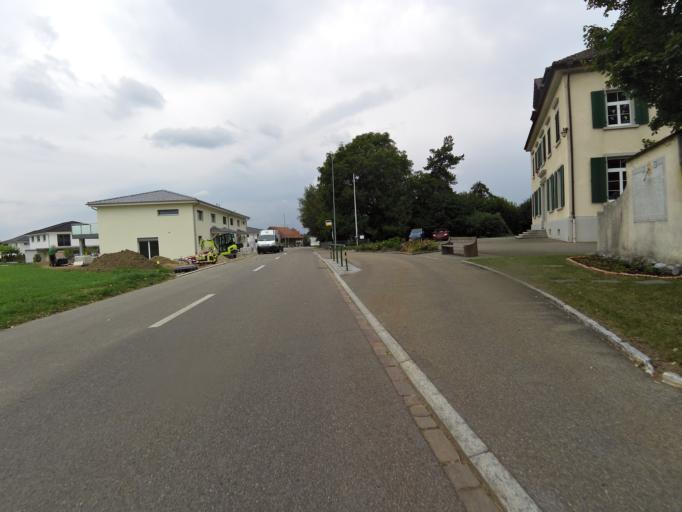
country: CH
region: Thurgau
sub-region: Frauenfeld District
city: Homburg
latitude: 47.6356
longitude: 9.0442
